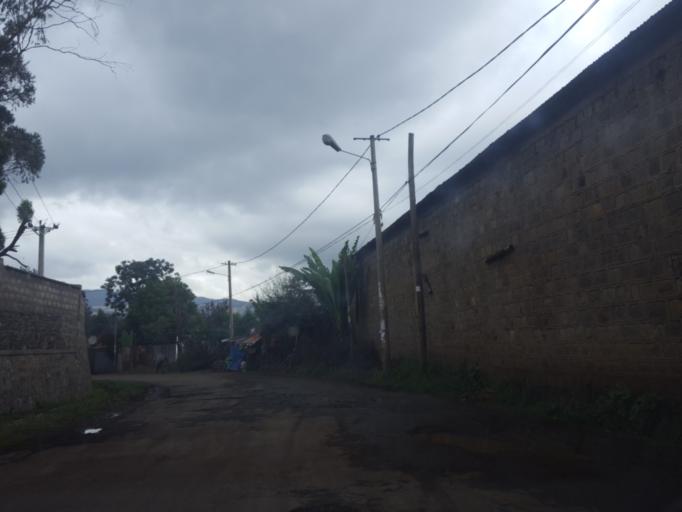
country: ET
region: Adis Abeba
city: Addis Ababa
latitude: 9.0487
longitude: 38.7656
